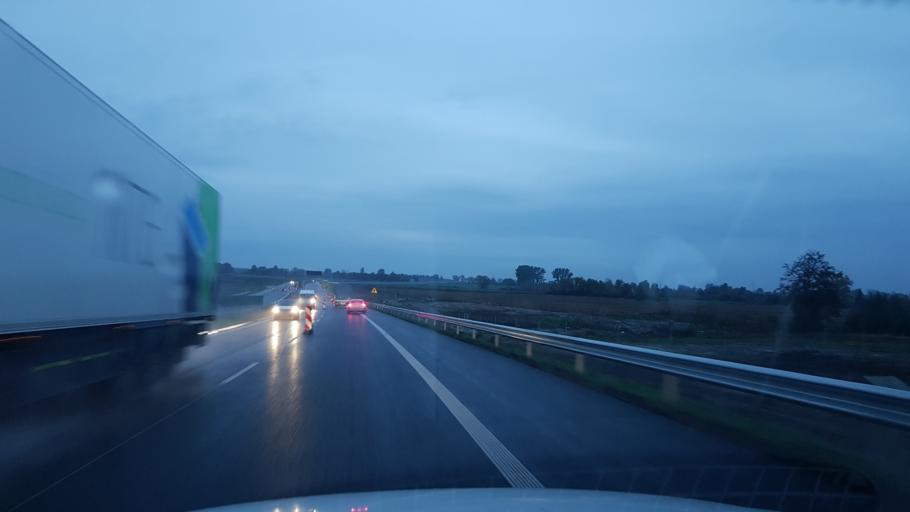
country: PL
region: West Pomeranian Voivodeship
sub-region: Powiat gryficki
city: Ploty
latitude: 53.8012
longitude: 15.2520
